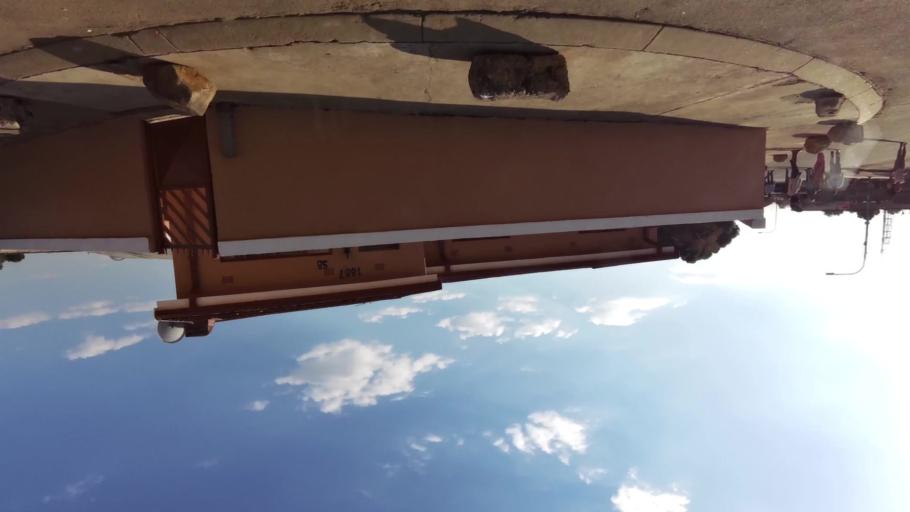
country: ZA
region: Gauteng
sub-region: City of Johannesburg Metropolitan Municipality
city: Soweto
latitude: -26.2205
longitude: 27.8727
